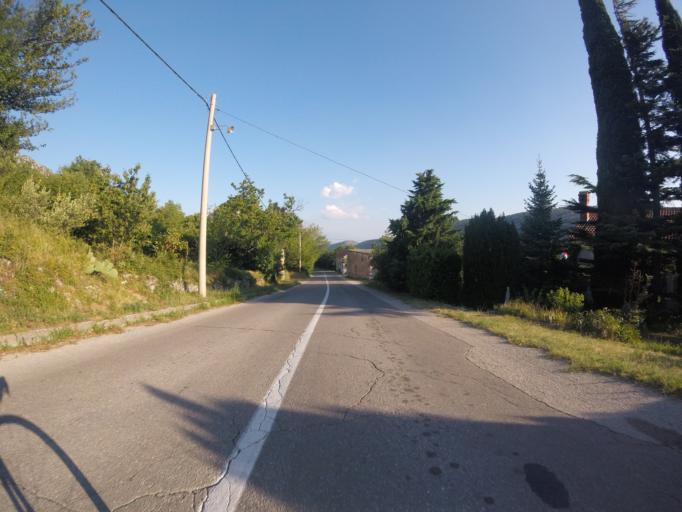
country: HR
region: Primorsko-Goranska
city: Selce
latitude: 45.1823
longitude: 14.7349
